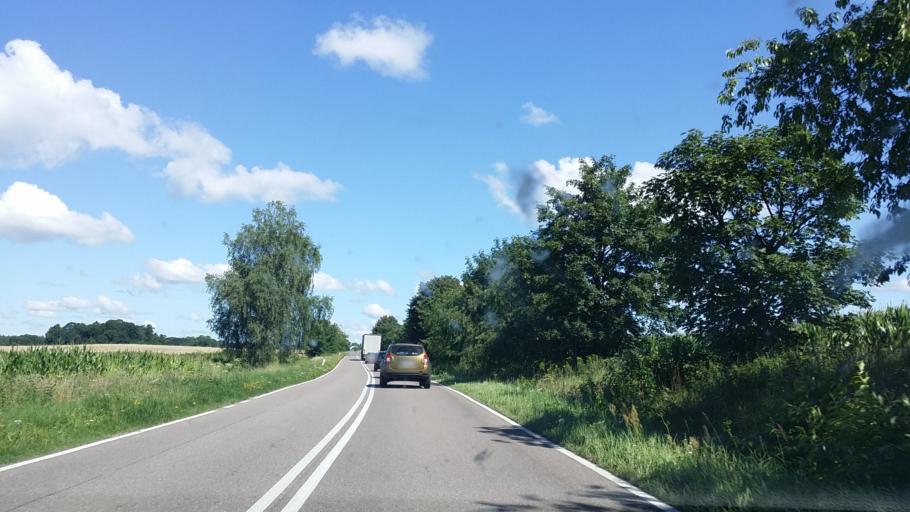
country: PL
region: West Pomeranian Voivodeship
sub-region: Powiat drawski
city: Kalisz Pomorski
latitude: 53.3302
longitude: 15.8962
